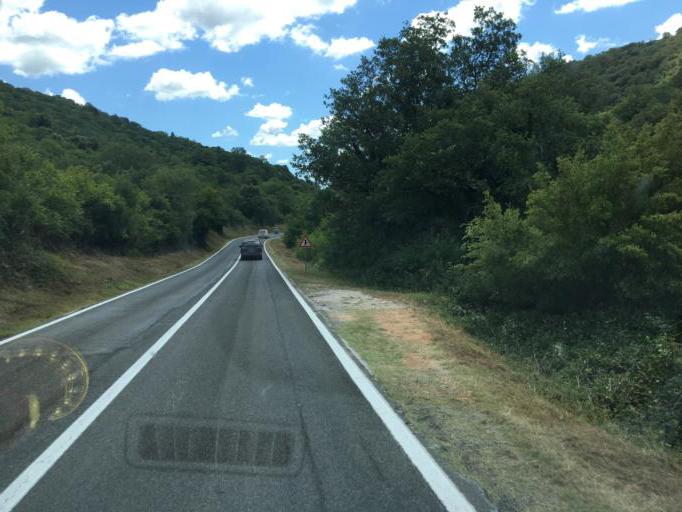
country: HR
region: Istarska
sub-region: Grad Rovinj
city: Rovinj
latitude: 45.1293
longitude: 13.7418
